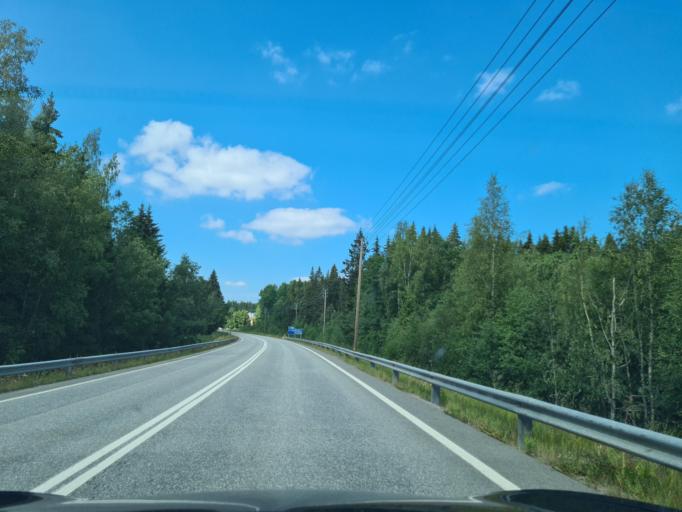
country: FI
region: Ostrobothnia
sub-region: Vaasa
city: Vaasa
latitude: 63.1900
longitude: 21.5642
